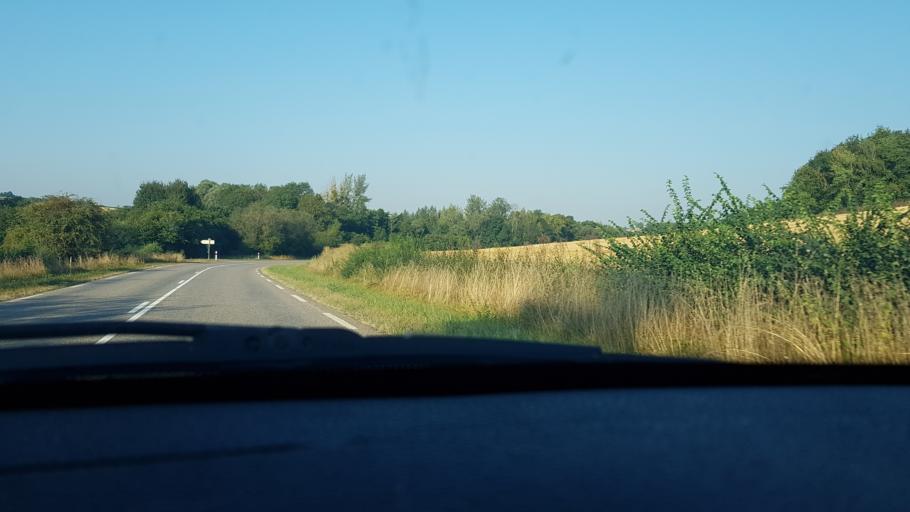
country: FR
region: Lorraine
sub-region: Departement des Vosges
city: Mirecourt
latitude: 48.3540
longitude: 6.1768
